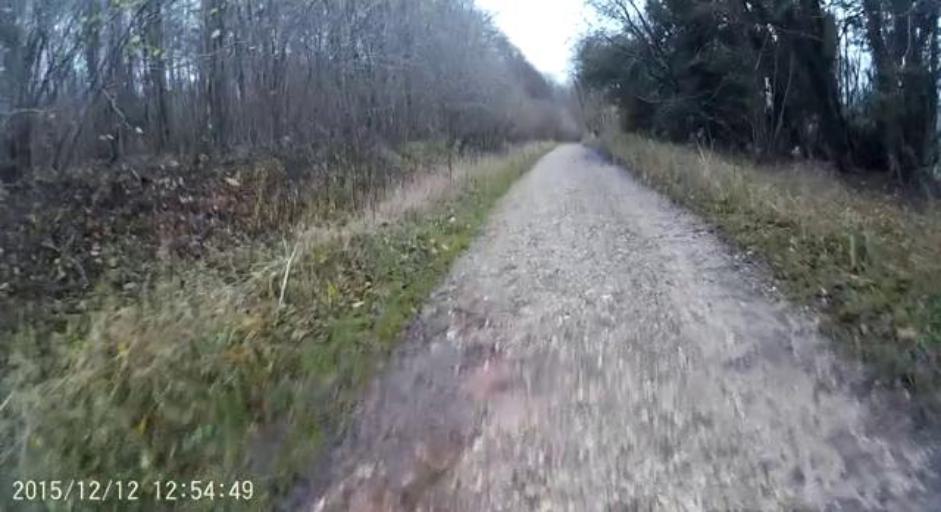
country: GB
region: England
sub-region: Hampshire
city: Petersfield
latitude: 50.9712
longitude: -0.9611
